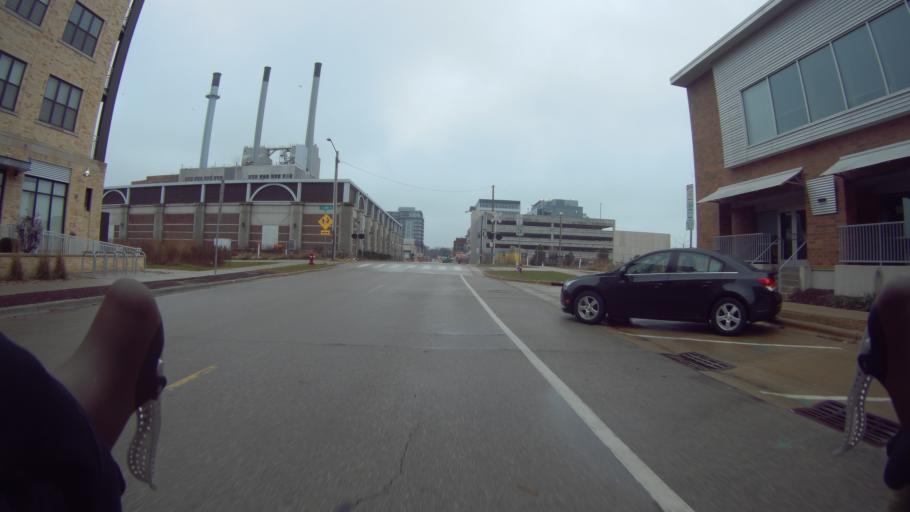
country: US
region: Wisconsin
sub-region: Dane County
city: Madison
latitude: 43.0787
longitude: -89.3722
